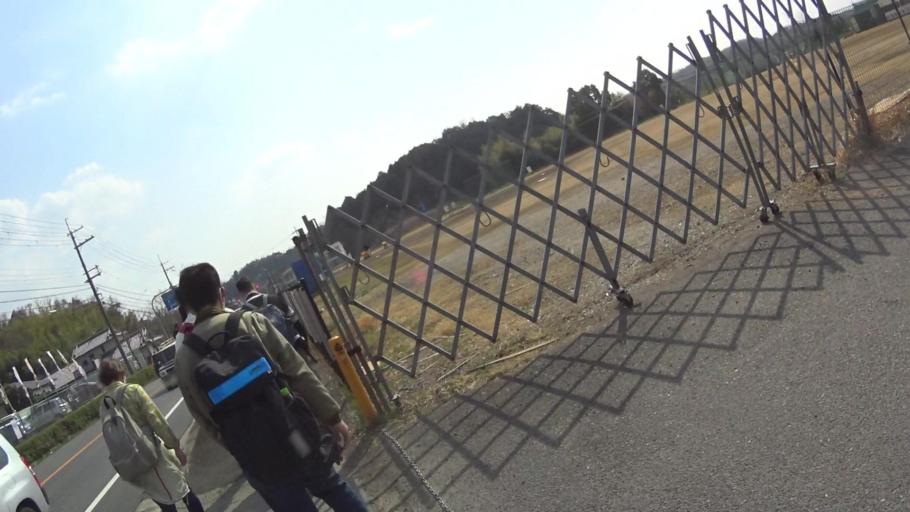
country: JP
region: Nara
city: Nara-shi
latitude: 34.7079
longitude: 135.8275
